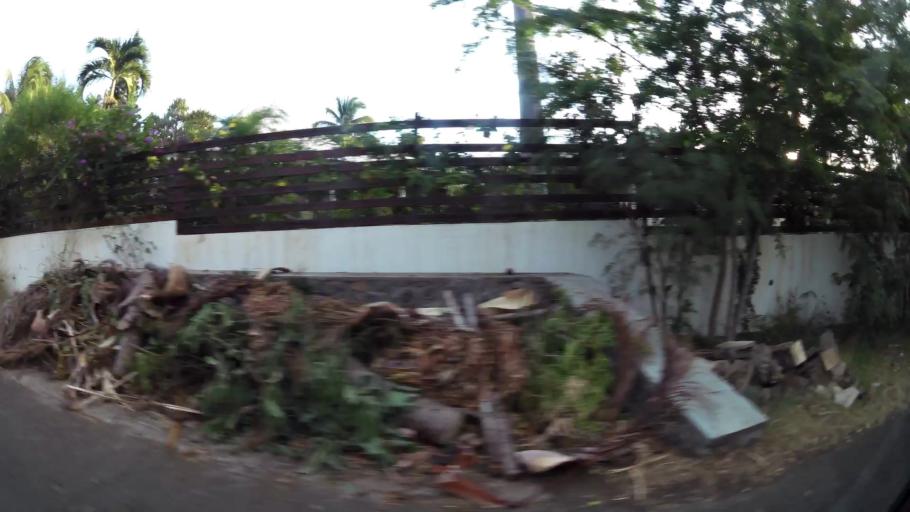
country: RE
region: Reunion
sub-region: Reunion
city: Saint-Paul
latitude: -21.0417
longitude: 55.2226
